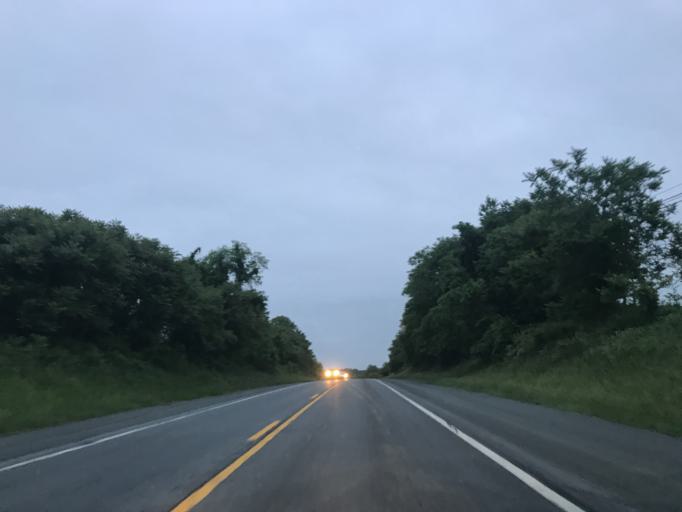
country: US
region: Maryland
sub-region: Frederick County
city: Linganore
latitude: 39.4000
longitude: -77.2599
